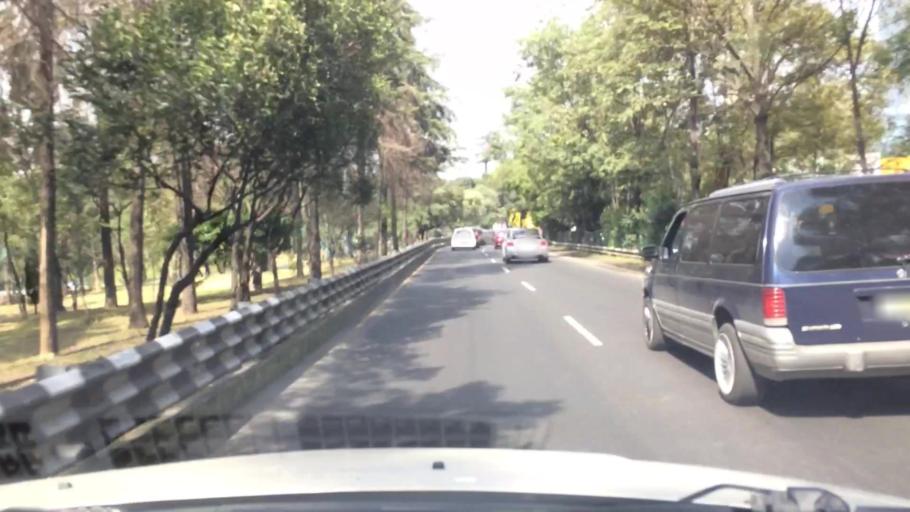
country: MX
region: Mexico City
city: Magdalena Contreras
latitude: 19.3040
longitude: -99.2059
